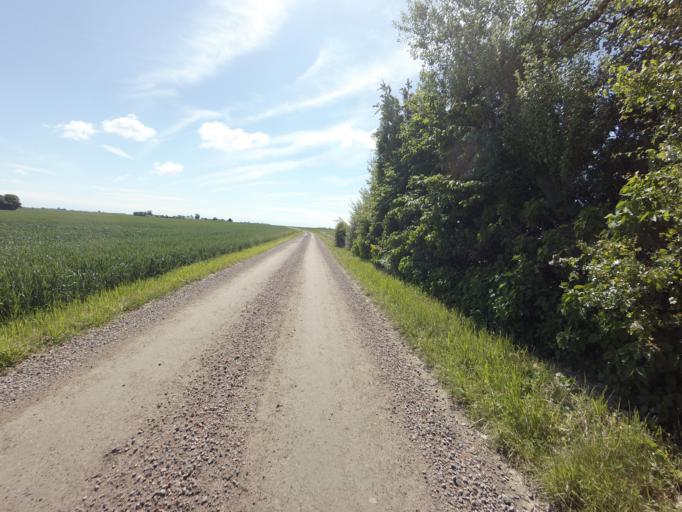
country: SE
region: Skane
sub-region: Trelleborgs Kommun
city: Skare
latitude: 55.4158
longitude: 13.0343
